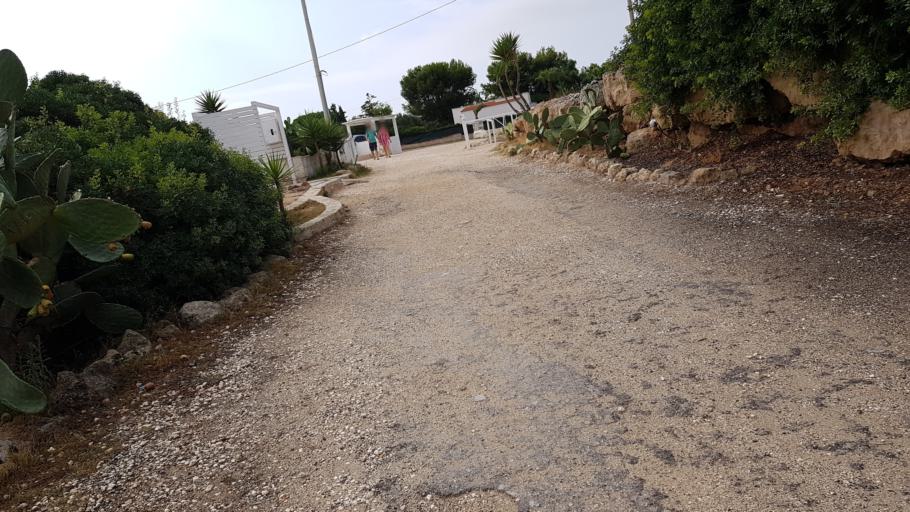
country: IT
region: Apulia
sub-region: Provincia di Bari
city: Monopoli
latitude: 40.9300
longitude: 17.3301
